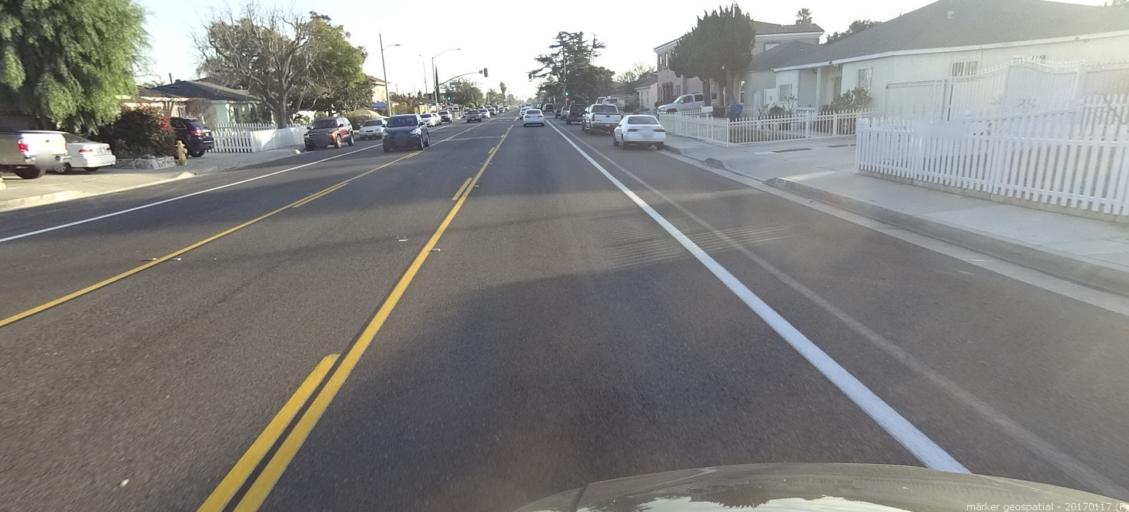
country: US
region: California
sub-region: Orange County
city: Midway City
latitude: 33.7496
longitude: -117.9810
